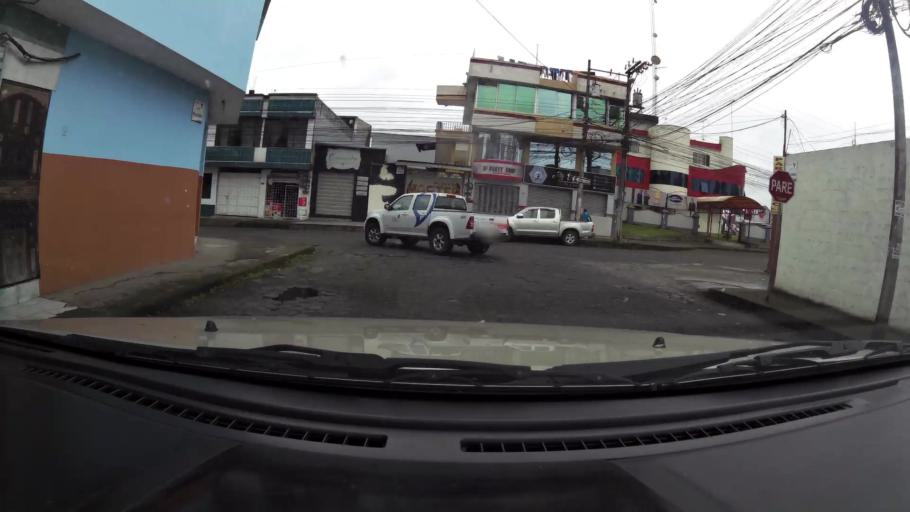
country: EC
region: Santo Domingo de los Tsachilas
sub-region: Canton Santo Domingo de los Colorados
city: Santo Domingo de los Colorados
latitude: -0.2506
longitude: -79.1642
